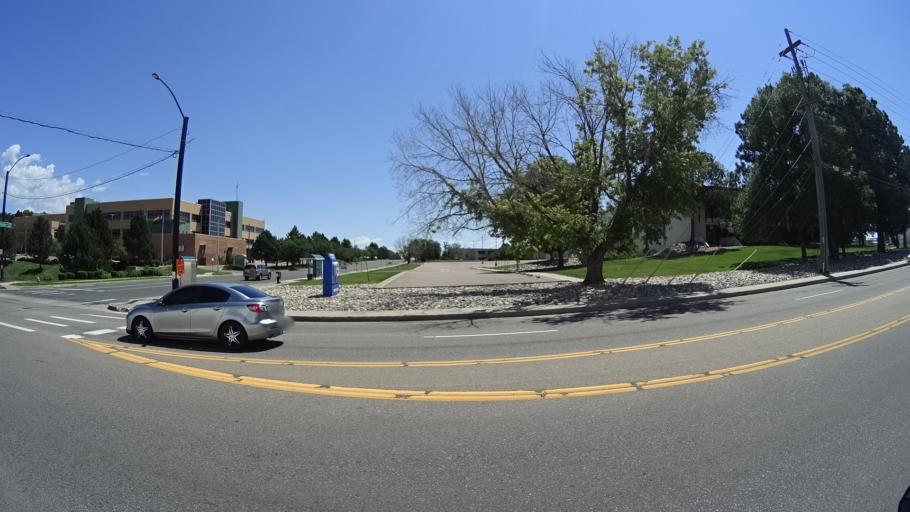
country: US
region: Colorado
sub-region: El Paso County
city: Colorado Springs
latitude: 38.8288
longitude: -104.7950
